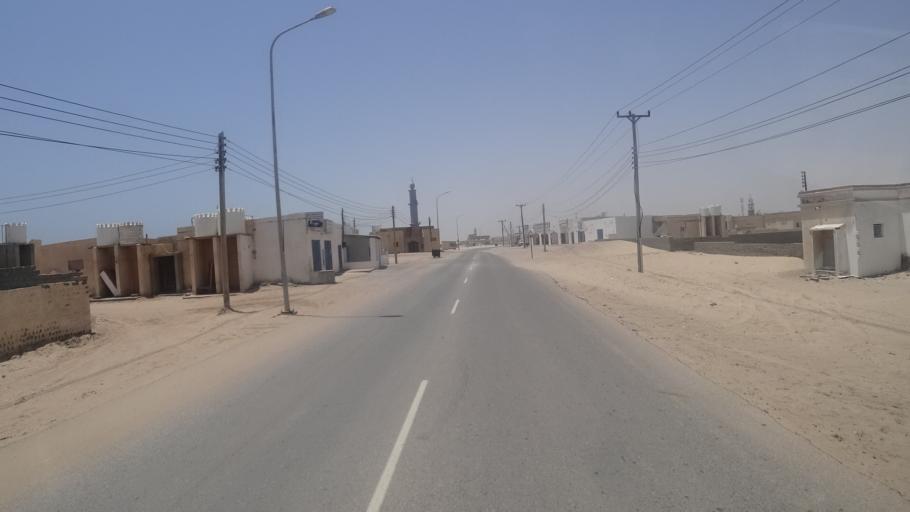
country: OM
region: Ash Sharqiyah
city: Sur
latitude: 22.0866
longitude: 59.6884
